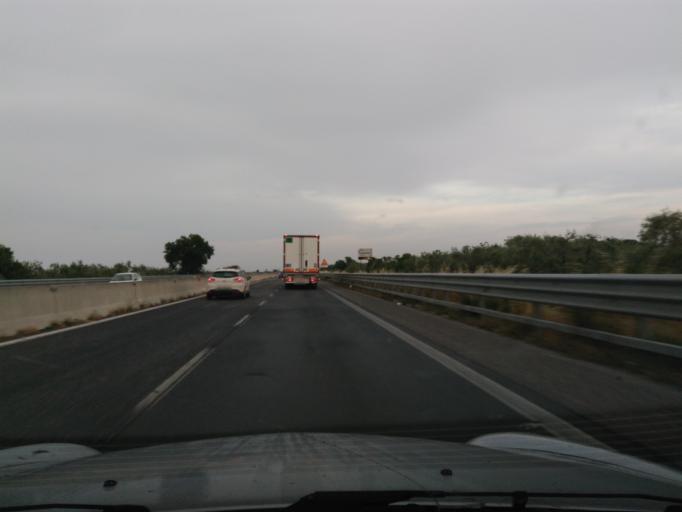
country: IT
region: Apulia
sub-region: Provincia di Bari
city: Giovinazzo
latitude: 41.1846
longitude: 16.6359
